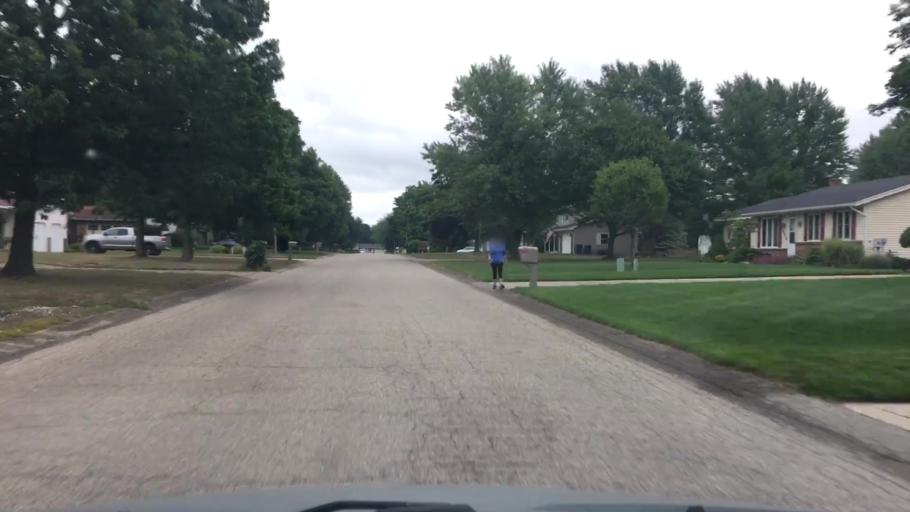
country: US
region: Michigan
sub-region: Ottawa County
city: Hudsonville
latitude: 42.9004
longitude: -85.8502
